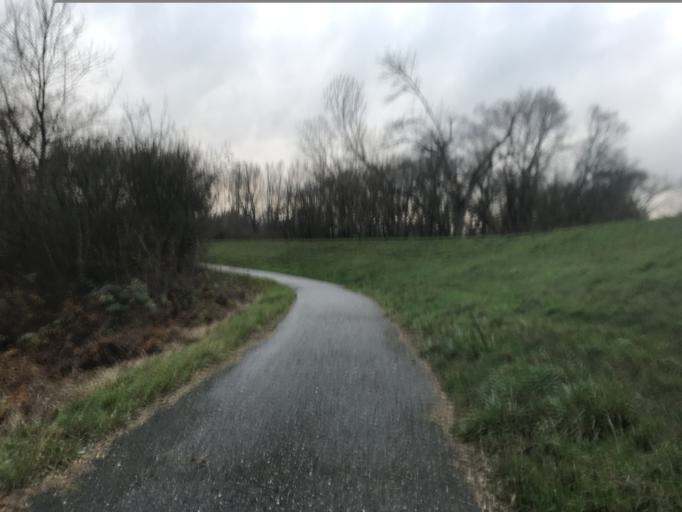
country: DE
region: Rheinland-Pfalz
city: Oestrich-Winkel
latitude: 49.9941
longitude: 8.0348
